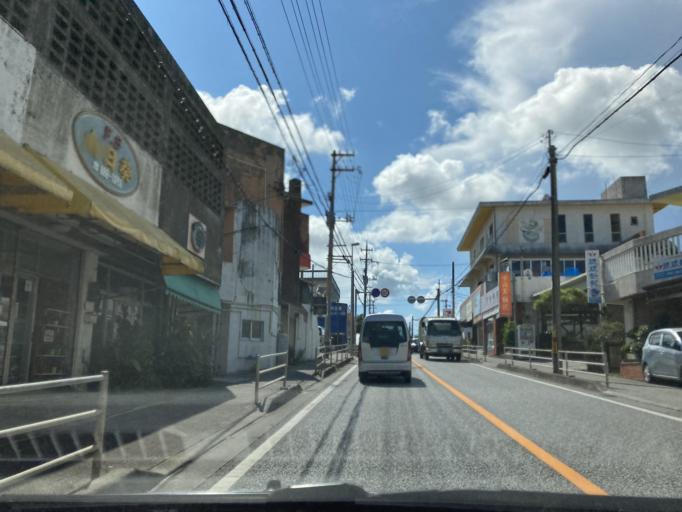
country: JP
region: Okinawa
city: Tomigusuku
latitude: 26.1866
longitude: 127.7108
